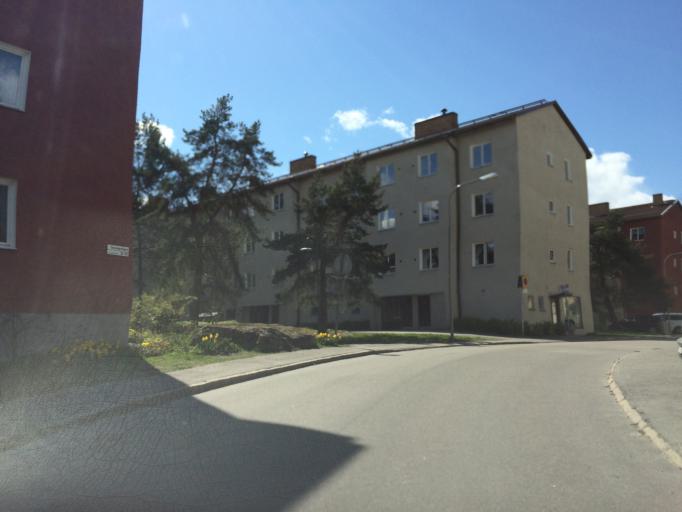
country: SE
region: Stockholm
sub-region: Huddinge Kommun
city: Segeltorp
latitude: 59.2945
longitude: 17.9739
